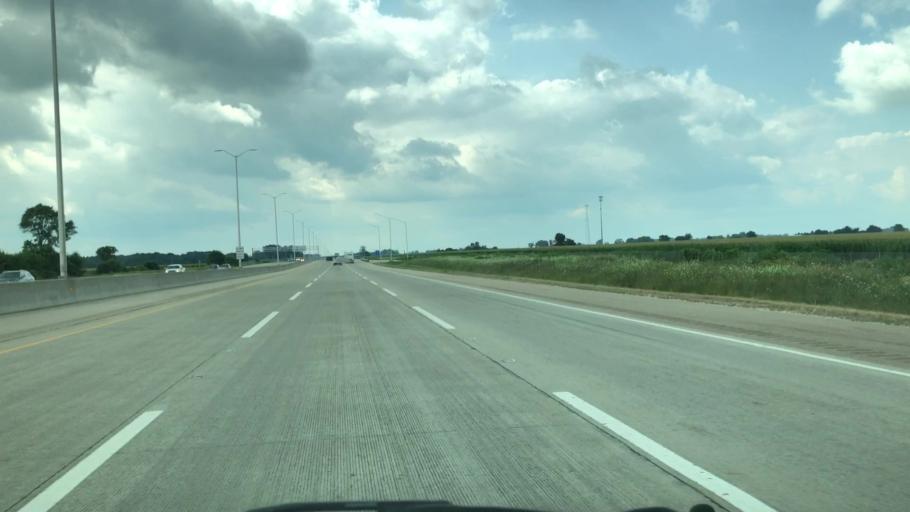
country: US
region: Illinois
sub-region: McHenry County
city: Marengo
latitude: 42.1731
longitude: -88.6046
